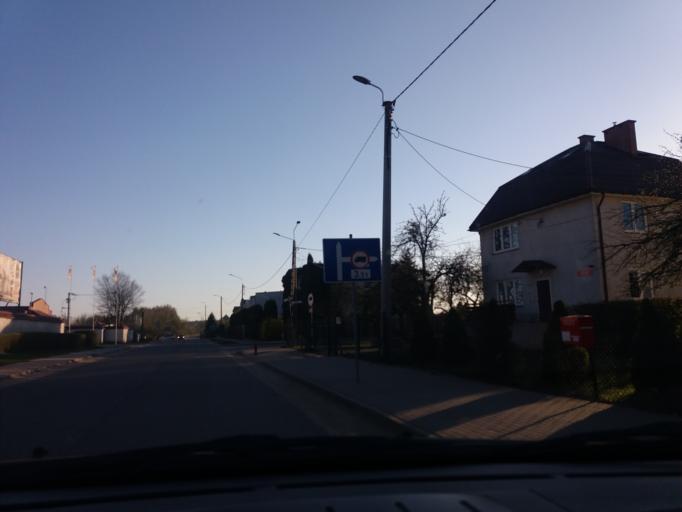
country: PL
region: Warmian-Masurian Voivodeship
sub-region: Powiat szczycienski
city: Szczytno
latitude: 53.5544
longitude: 20.9833
